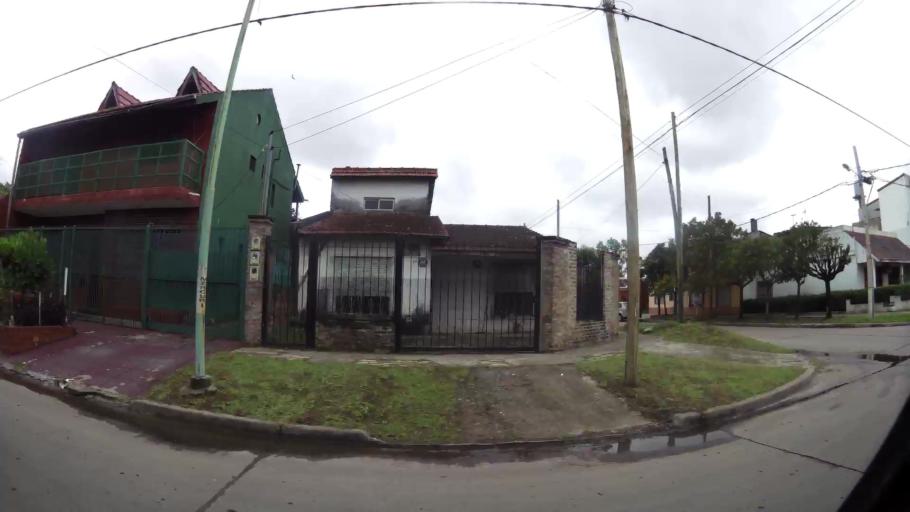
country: AR
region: Buenos Aires
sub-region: Partido de Lomas de Zamora
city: Lomas de Zamora
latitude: -34.7506
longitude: -58.3682
